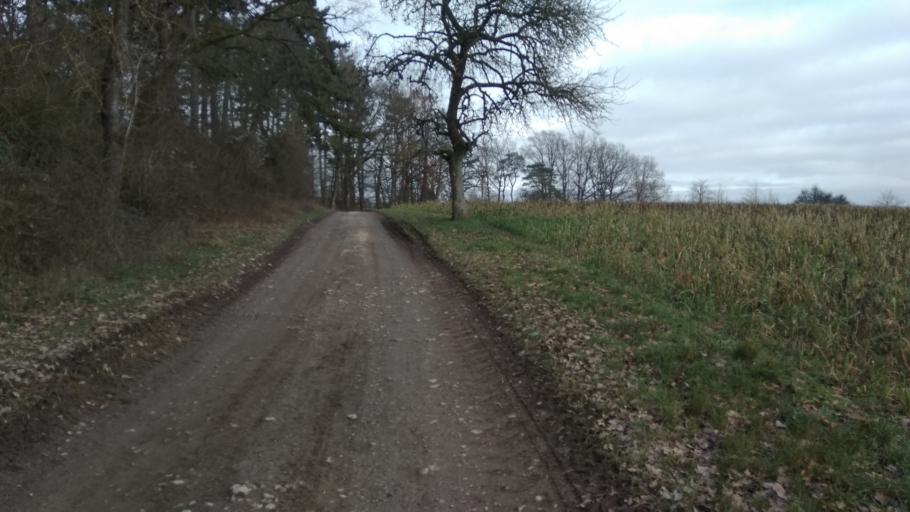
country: DE
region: Baden-Wuerttemberg
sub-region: Karlsruhe Region
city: Mosbach
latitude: 49.3628
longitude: 9.1746
